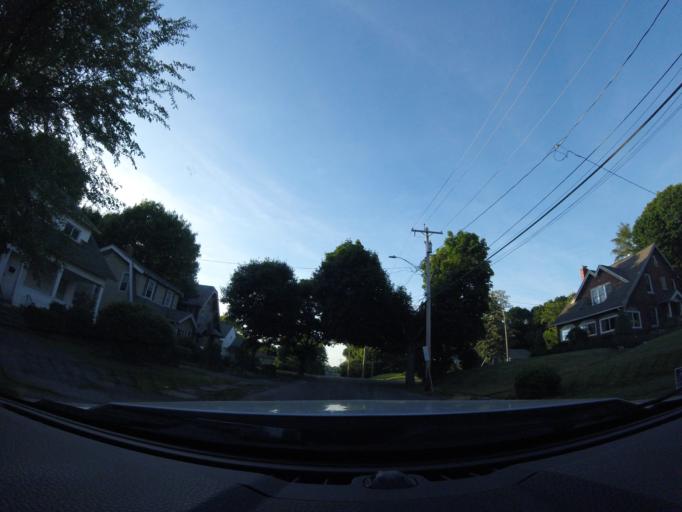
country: US
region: New York
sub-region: Onondaga County
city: East Syracuse
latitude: 43.0488
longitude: -76.1083
